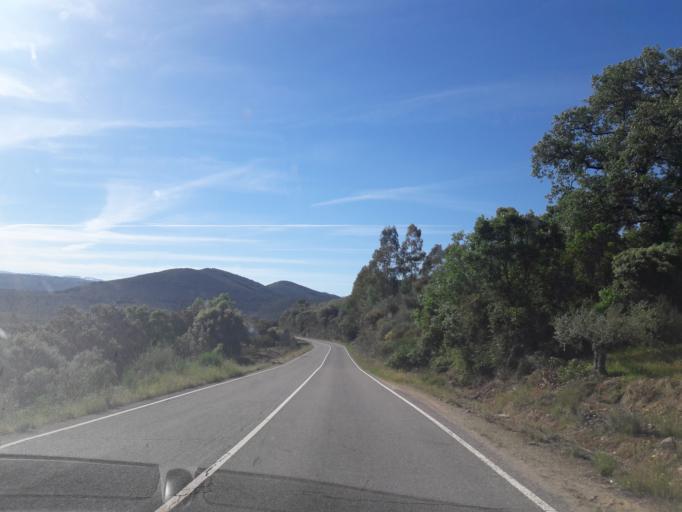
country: ES
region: Castille and Leon
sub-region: Provincia de Salamanca
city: Sotoserrano
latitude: 40.4232
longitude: -6.0378
